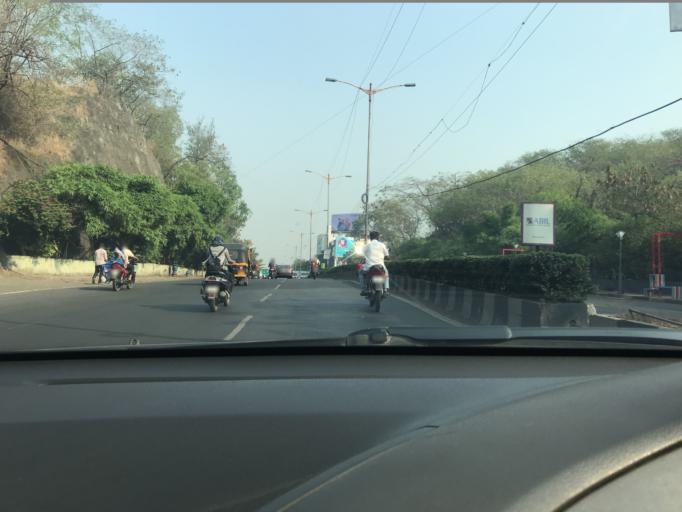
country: IN
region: Maharashtra
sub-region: Pune Division
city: Shivaji Nagar
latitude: 18.5228
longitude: 73.8295
